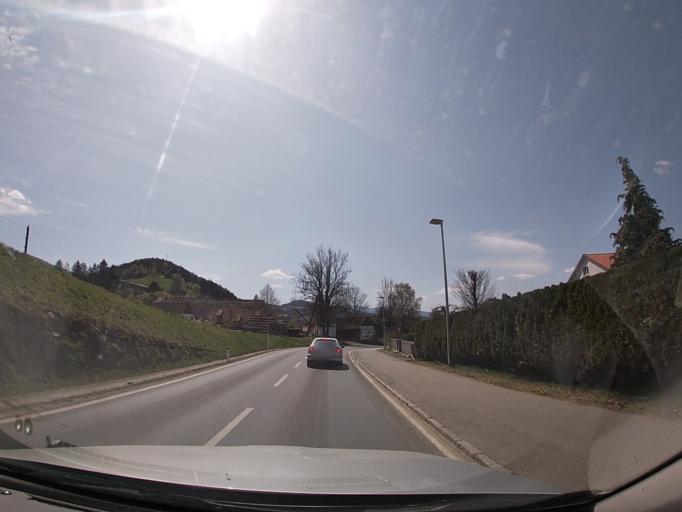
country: AT
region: Styria
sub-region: Politischer Bezirk Murtal
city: Sankt Margarethen bei Knittelfeld
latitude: 47.2176
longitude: 14.8485
